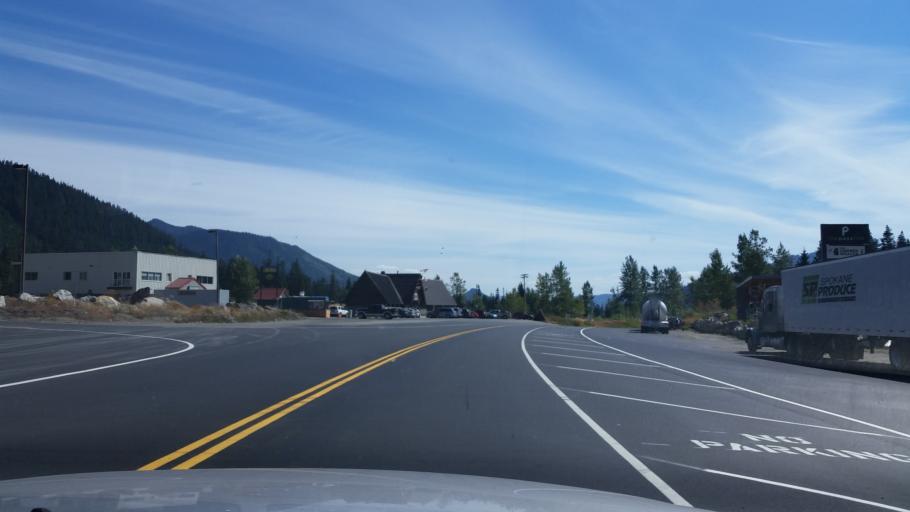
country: US
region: Washington
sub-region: King County
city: Tanner
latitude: 47.4221
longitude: -121.4124
